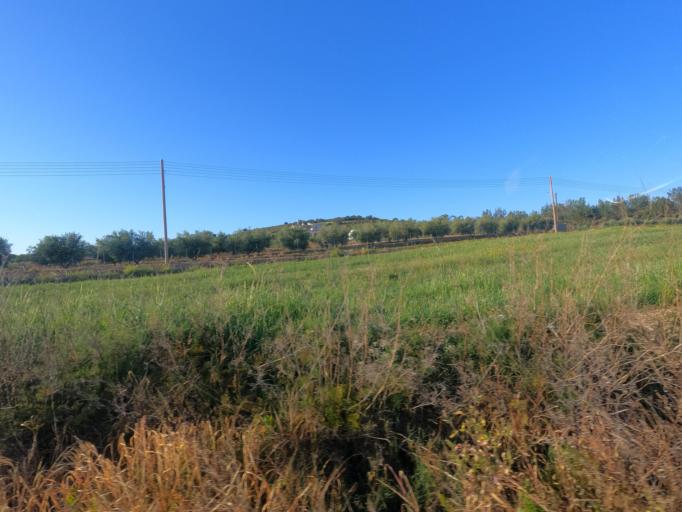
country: CY
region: Pafos
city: Polis
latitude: 35.0226
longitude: 32.4037
